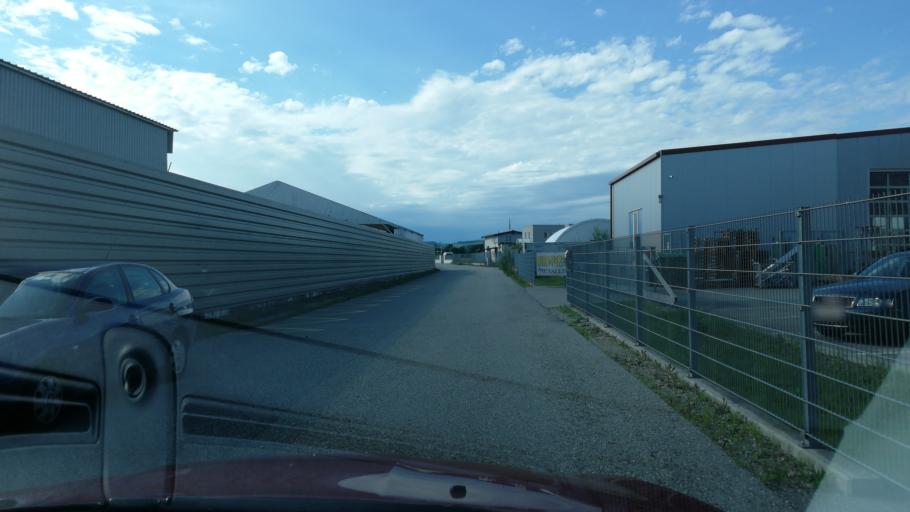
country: AT
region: Upper Austria
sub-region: Wels-Land
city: Holzhausen
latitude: 48.1971
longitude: 14.0868
